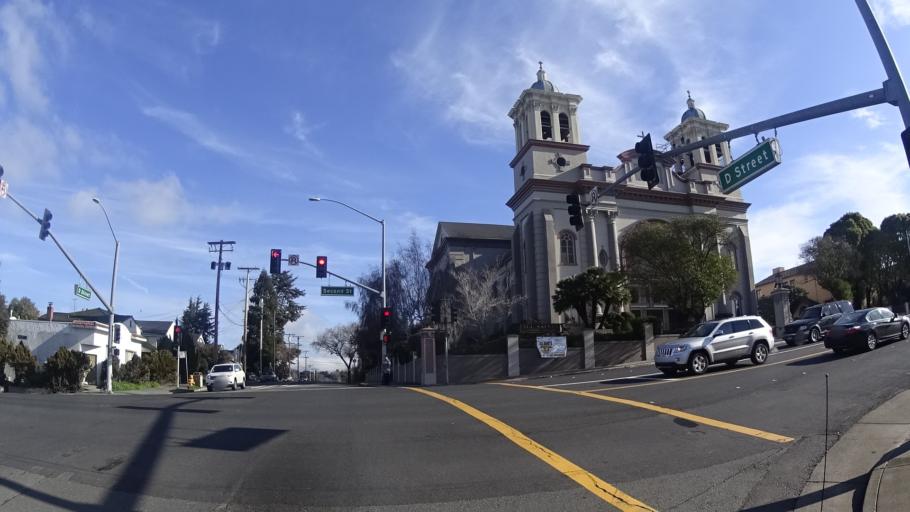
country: US
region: California
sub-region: Alameda County
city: Hayward
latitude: 37.6730
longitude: -122.0775
